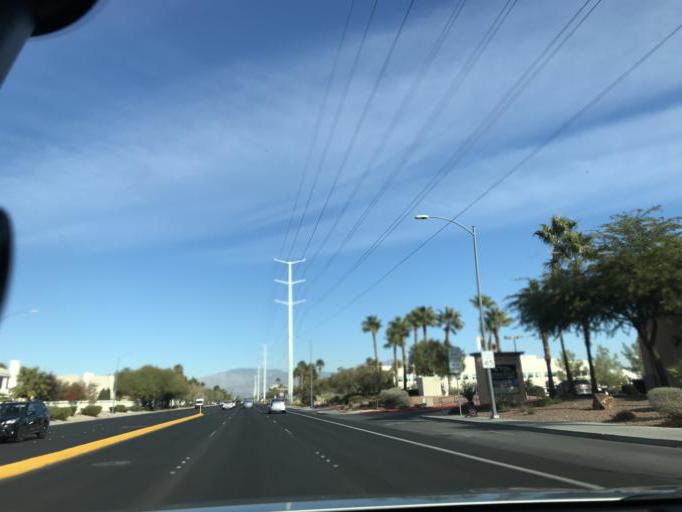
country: US
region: Nevada
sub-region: Clark County
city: Spring Valley
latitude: 36.2038
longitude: -115.2606
